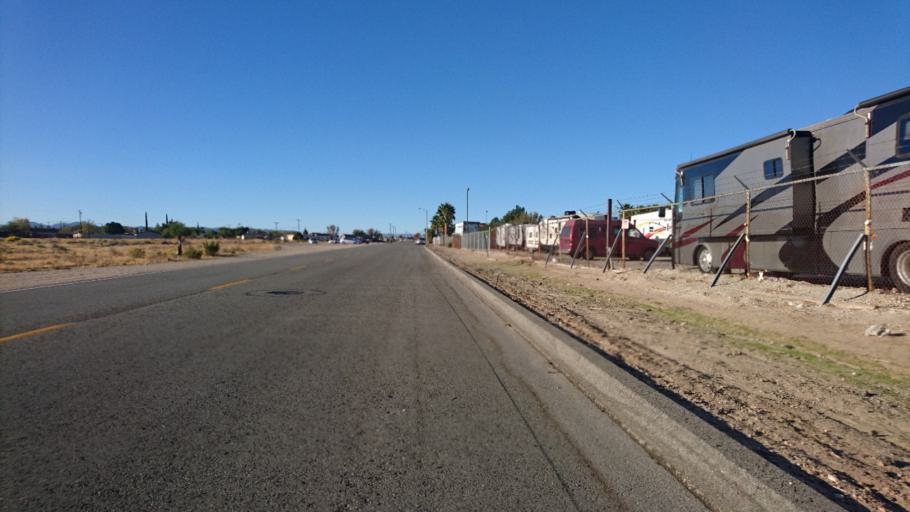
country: US
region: California
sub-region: San Bernardino County
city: Mountain View Acres
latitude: 34.4657
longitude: -117.3483
